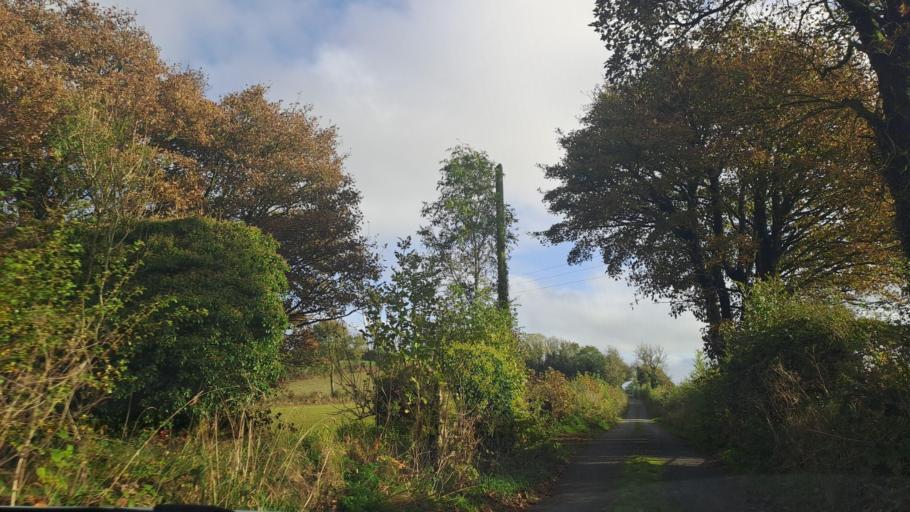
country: IE
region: Ulster
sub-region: County Monaghan
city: Carrickmacross
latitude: 54.0203
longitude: -6.7633
